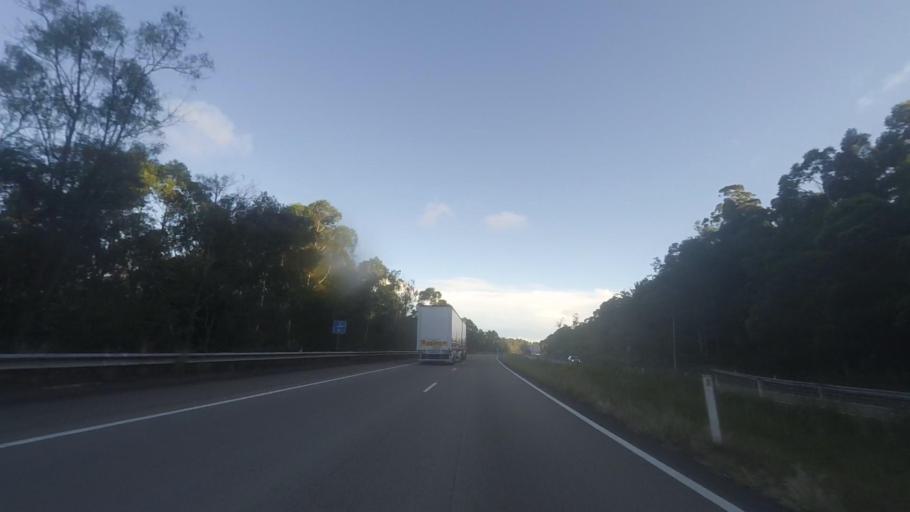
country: AU
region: New South Wales
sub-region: Great Lakes
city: Bulahdelah
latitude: -32.2866
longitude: 152.3406
